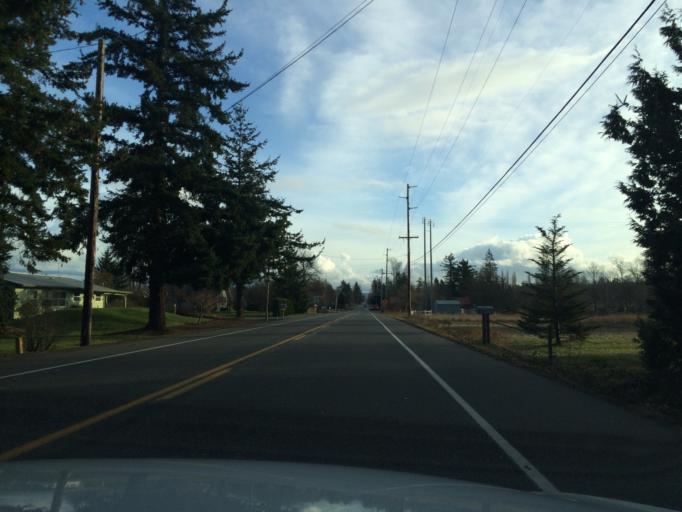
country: US
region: Washington
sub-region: Whatcom County
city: Marietta-Alderwood
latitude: 48.8191
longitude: -122.5300
